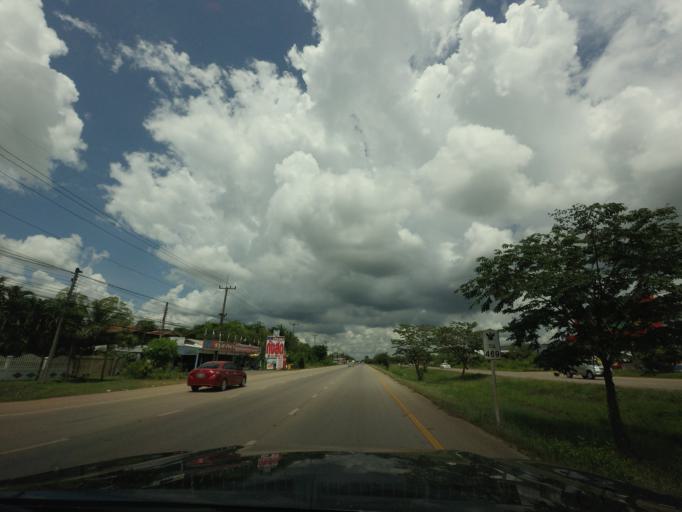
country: TH
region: Changwat Udon Thani
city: Udon Thani
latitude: 17.5310
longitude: 102.7997
